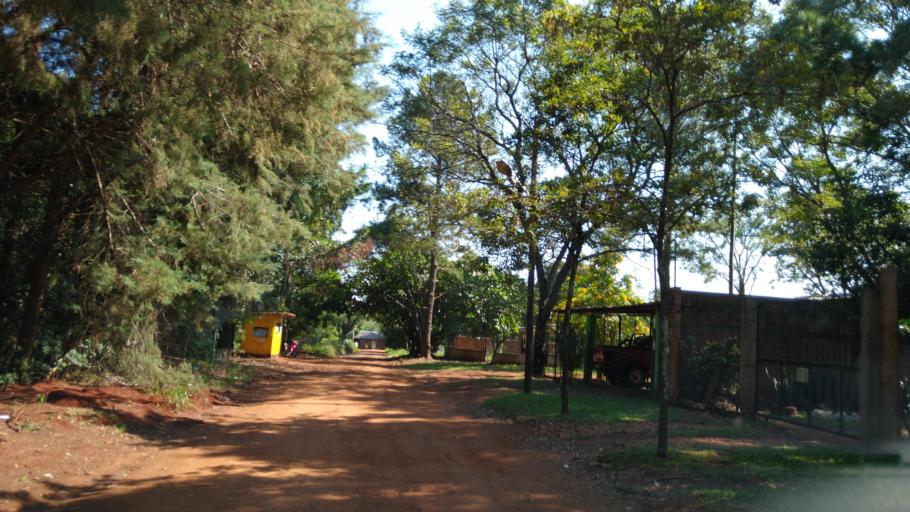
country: AR
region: Misiones
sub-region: Departamento de Capital
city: Posadas
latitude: -27.4067
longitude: -55.9767
